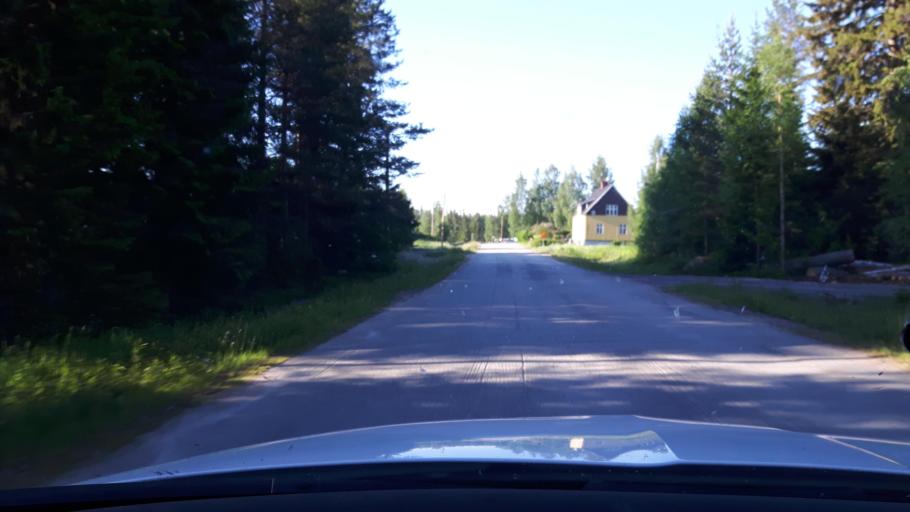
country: SE
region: Gaevleborg
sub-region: Ljusdals Kommun
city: Farila
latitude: 62.0027
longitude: 15.8379
